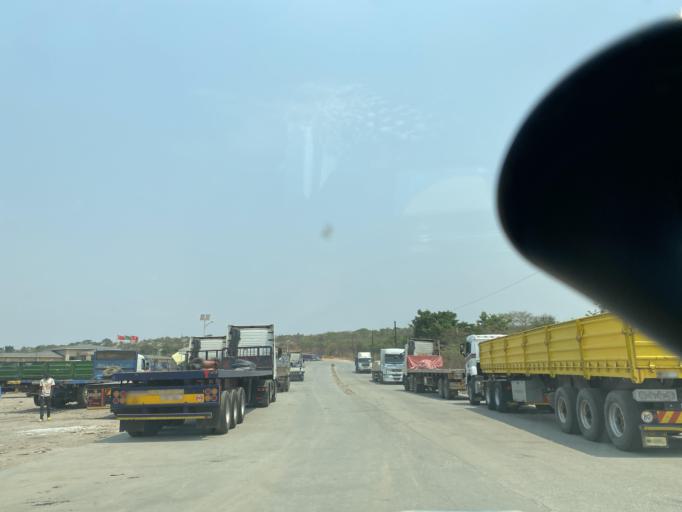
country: ZM
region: Lusaka
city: Lusaka
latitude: -15.5522
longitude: 28.4830
